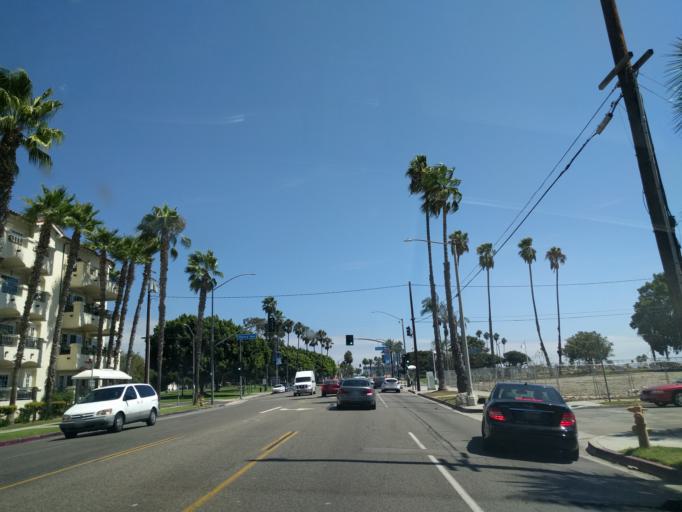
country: US
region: California
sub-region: Los Angeles County
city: Long Beach
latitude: 33.7645
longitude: -118.1692
